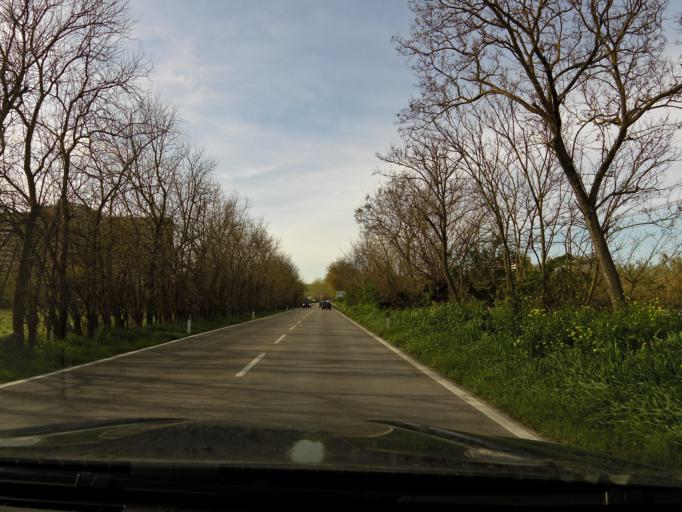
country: IT
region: The Marches
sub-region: Provincia di Macerata
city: Porto Recanati
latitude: 43.4157
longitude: 13.6698
